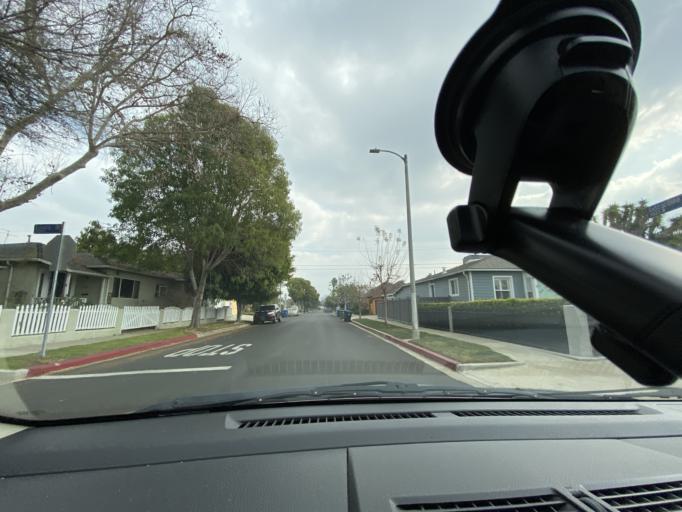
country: US
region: California
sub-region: Los Angeles County
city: Culver City
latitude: 34.0354
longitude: -118.3971
